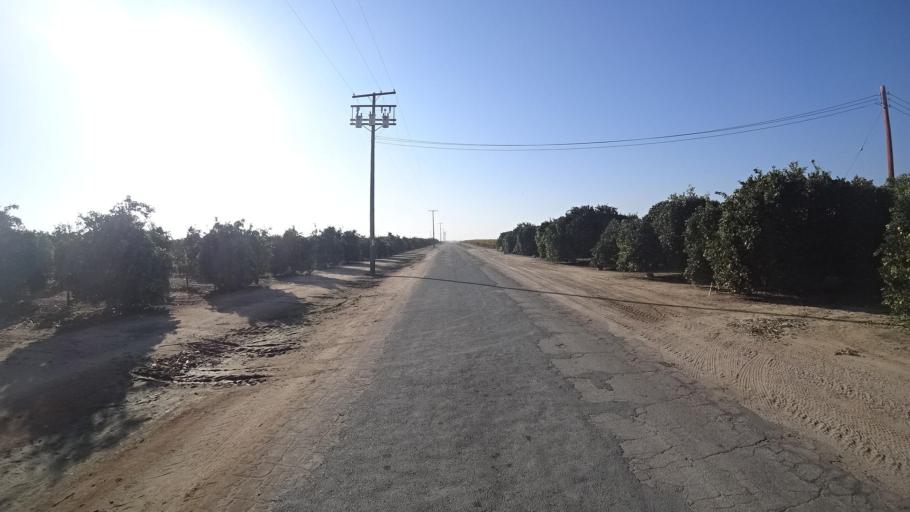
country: US
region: California
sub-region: Tulare County
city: Richgrove
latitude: 35.7758
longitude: -119.1607
